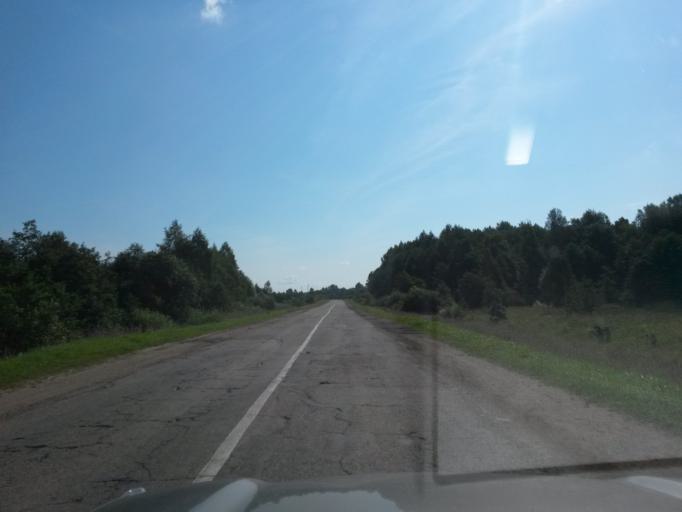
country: RU
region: Jaroslavl
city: Gavrilov-Yam
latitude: 57.3063
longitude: 39.9787
